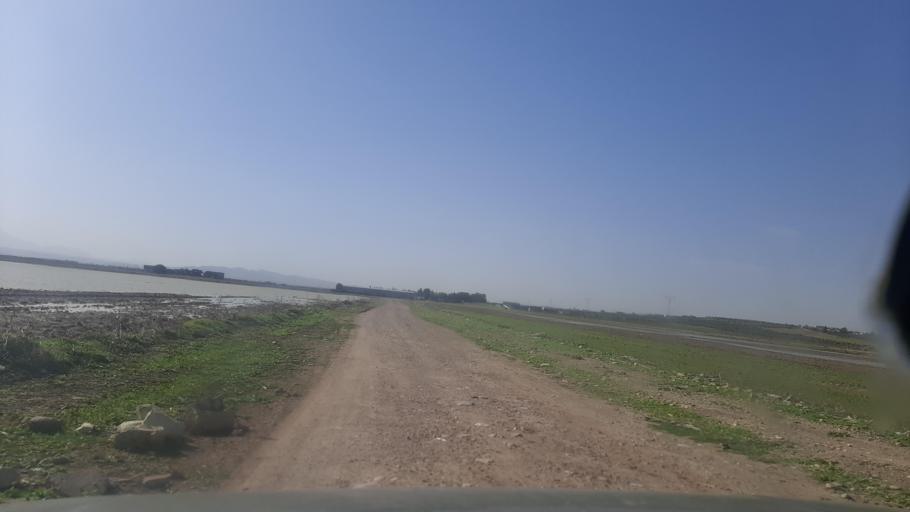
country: TN
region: Tunis
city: La Mohammedia
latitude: 36.6508
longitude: 10.0880
